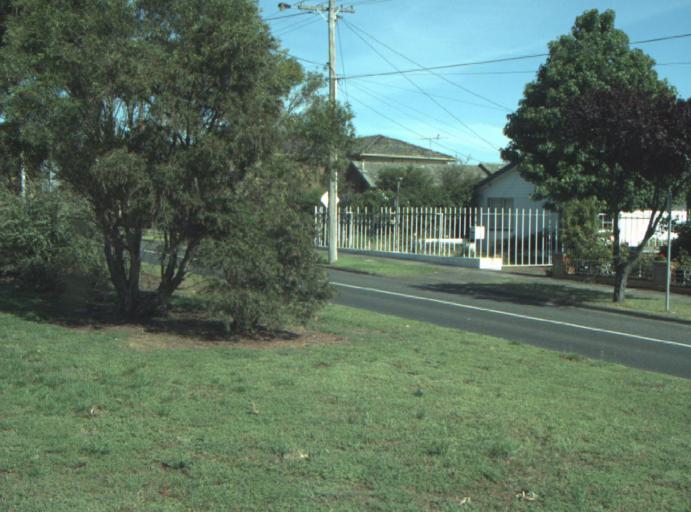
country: AU
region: Victoria
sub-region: Greater Geelong
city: Bell Post Hill
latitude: -38.0979
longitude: 144.3287
